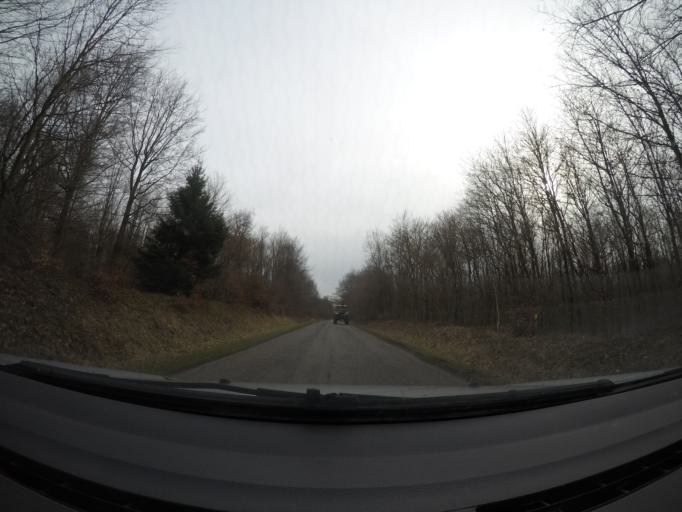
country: BE
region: Wallonia
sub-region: Province du Luxembourg
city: Martelange
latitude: 49.7855
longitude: 5.6876
